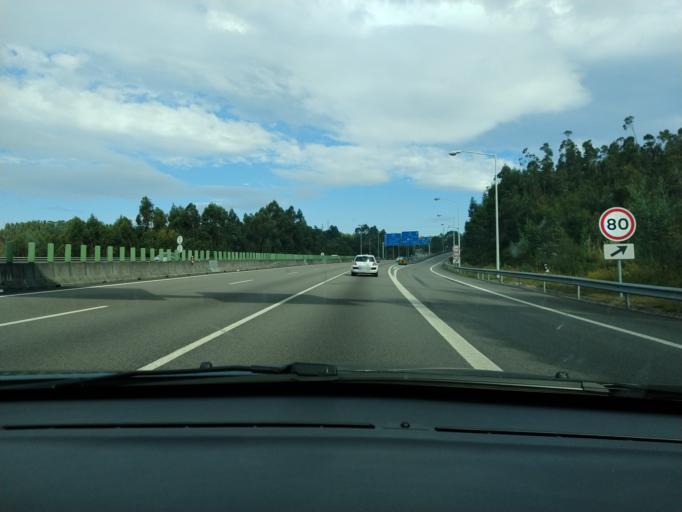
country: PT
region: Porto
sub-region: Vila Nova de Gaia
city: Perozinho
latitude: 41.0672
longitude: -8.5816
